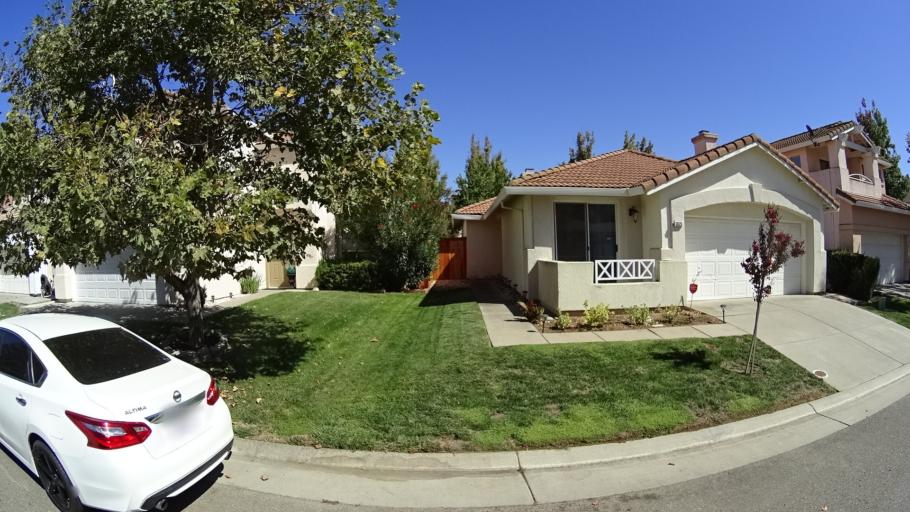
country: US
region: California
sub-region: Sacramento County
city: Laguna
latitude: 38.4202
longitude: -121.4643
